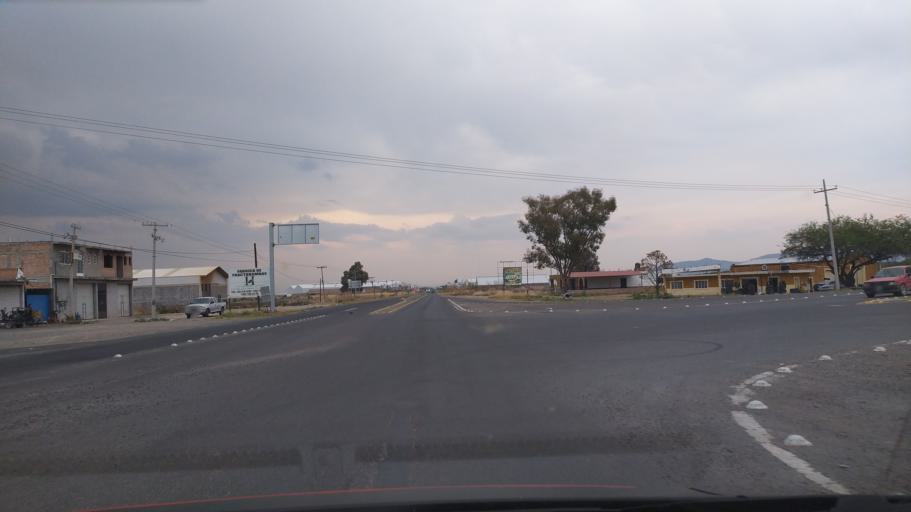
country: MX
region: Guanajuato
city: Ciudad Manuel Doblado
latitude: 20.7409
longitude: -101.9314
